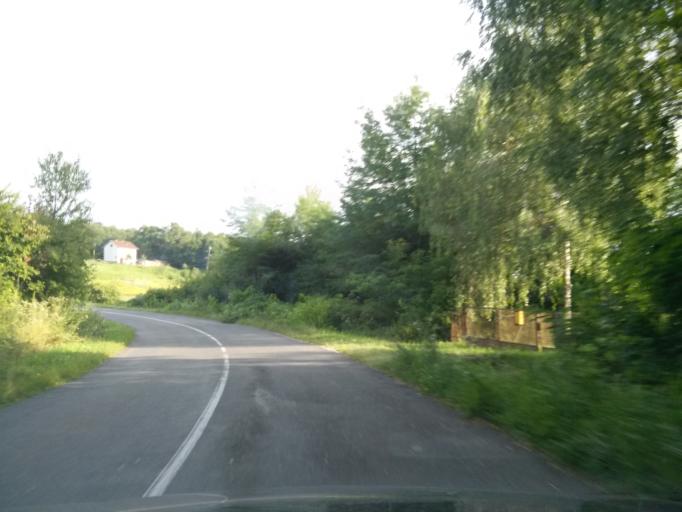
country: HR
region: Sisacko-Moslavacka
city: Gvozd
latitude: 45.3824
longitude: 15.9146
